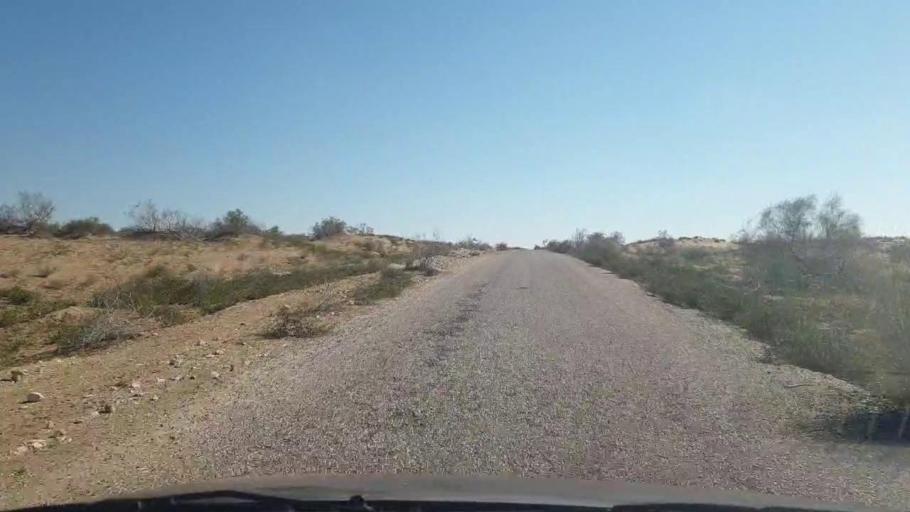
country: PK
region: Sindh
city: Bozdar
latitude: 27.0051
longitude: 68.8037
